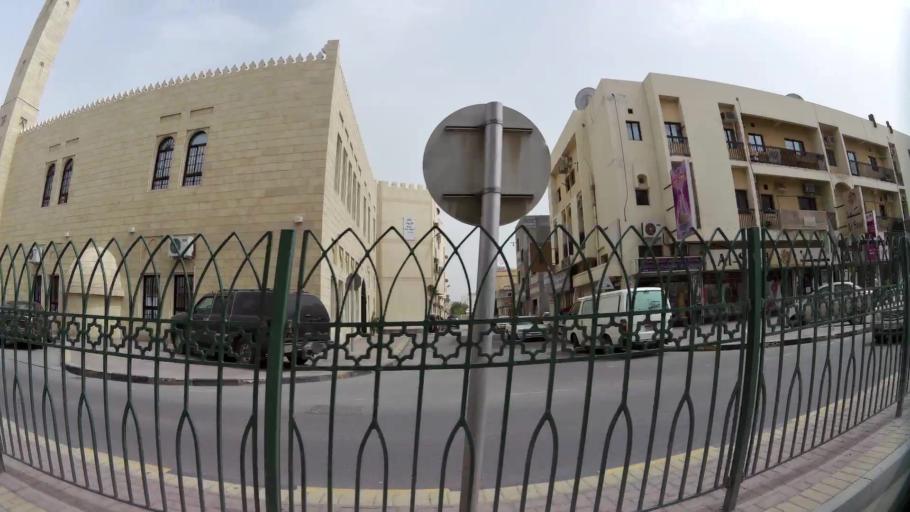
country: BH
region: Northern
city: Madinat `Isa
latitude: 26.1822
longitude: 50.5458
